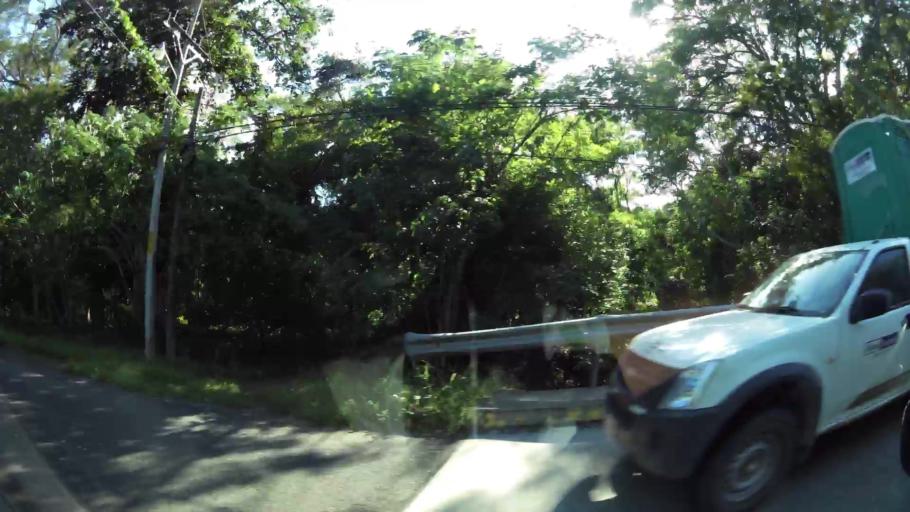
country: CR
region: Guanacaste
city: Sardinal
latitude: 10.5856
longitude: -85.6584
